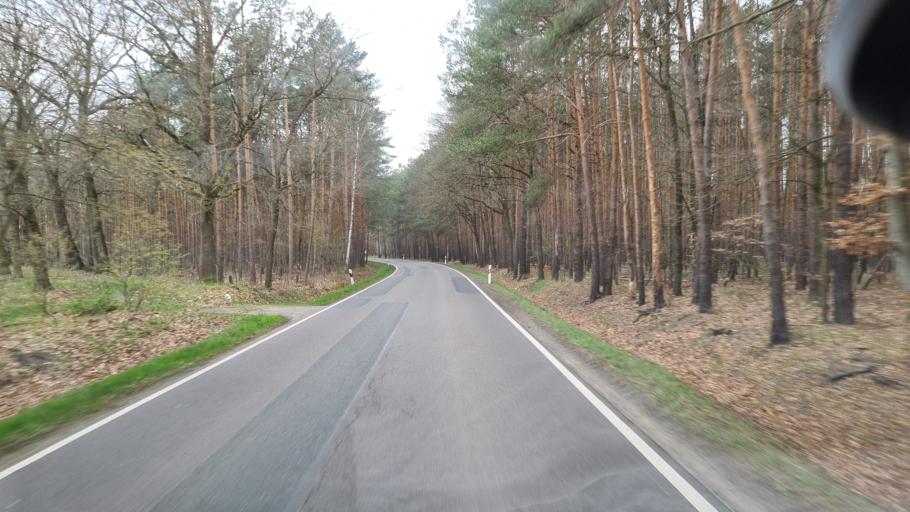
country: DE
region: Brandenburg
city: Schwarzbach
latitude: 51.4506
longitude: 13.9677
